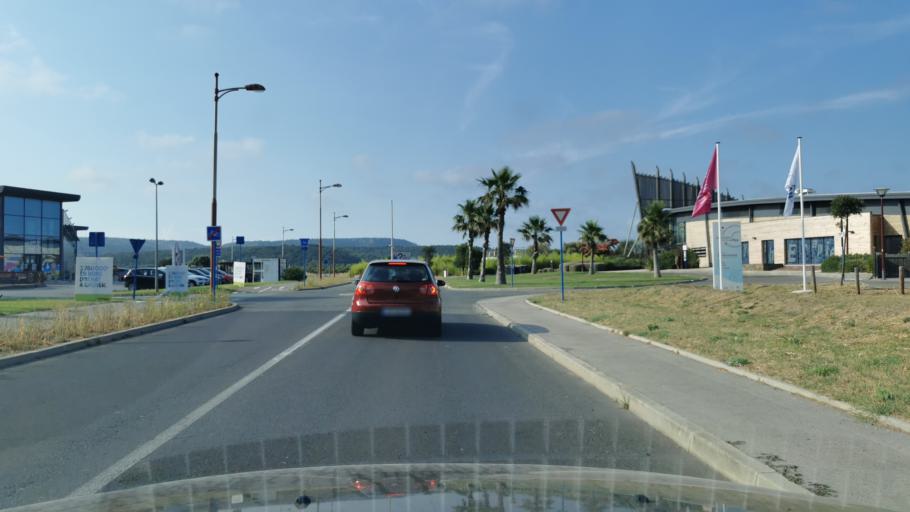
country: FR
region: Languedoc-Roussillon
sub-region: Departement de l'Aude
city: Gruissan
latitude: 43.1175
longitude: 3.1127
